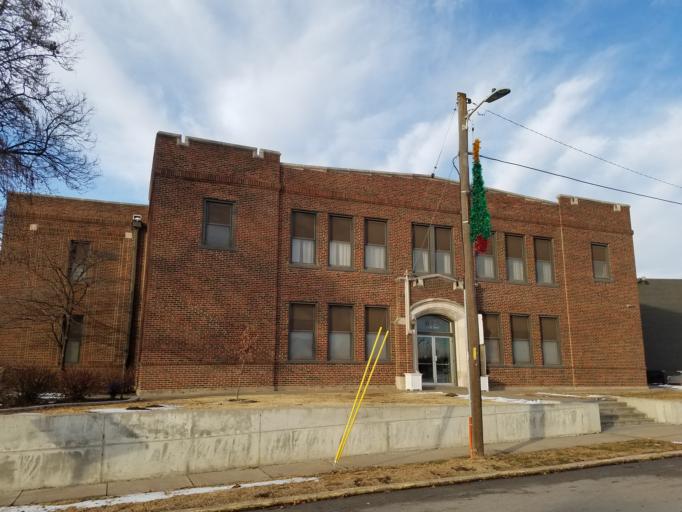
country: US
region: Missouri
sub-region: Saline County
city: Sweet Springs
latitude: 38.9634
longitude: -93.4168
